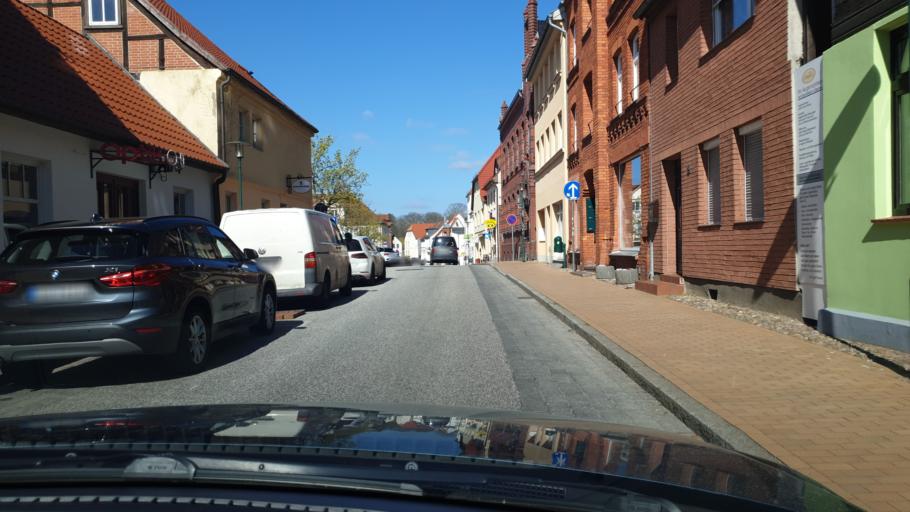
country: DE
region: Mecklenburg-Vorpommern
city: Crivitz
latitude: 53.5771
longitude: 11.6508
